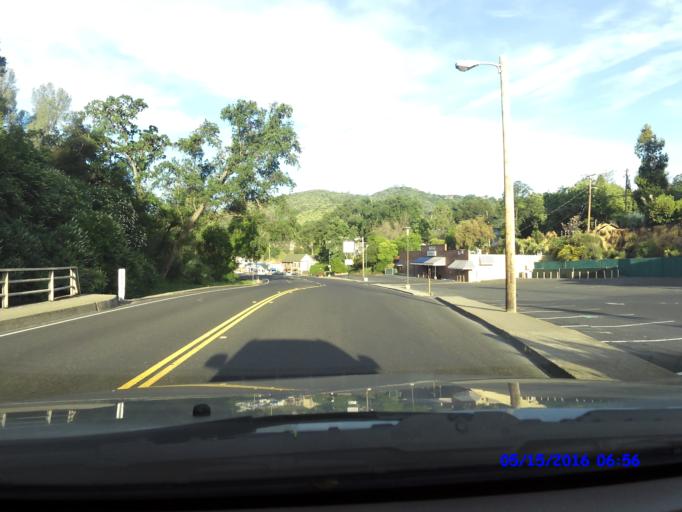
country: US
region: California
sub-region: Tuolumne County
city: Sonora
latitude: 37.9828
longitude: -120.3851
